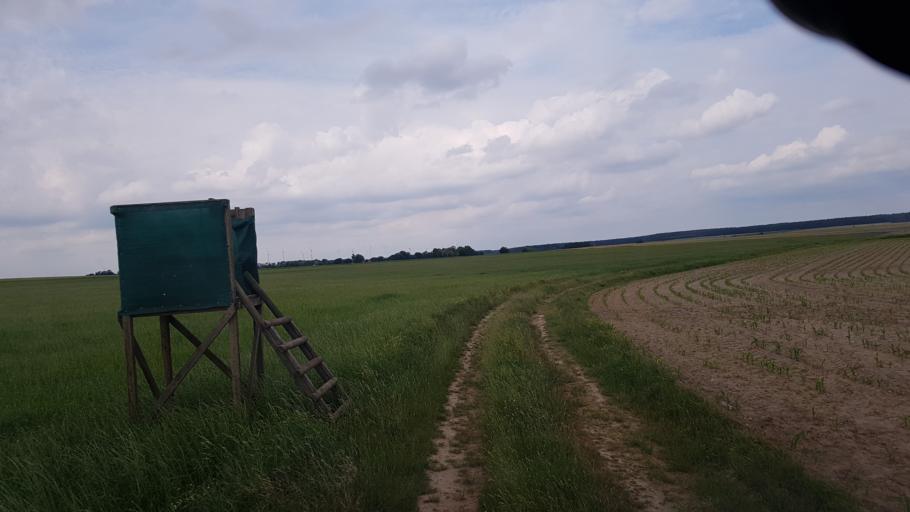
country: DE
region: Brandenburg
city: Dahme
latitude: 51.8817
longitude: 13.3986
